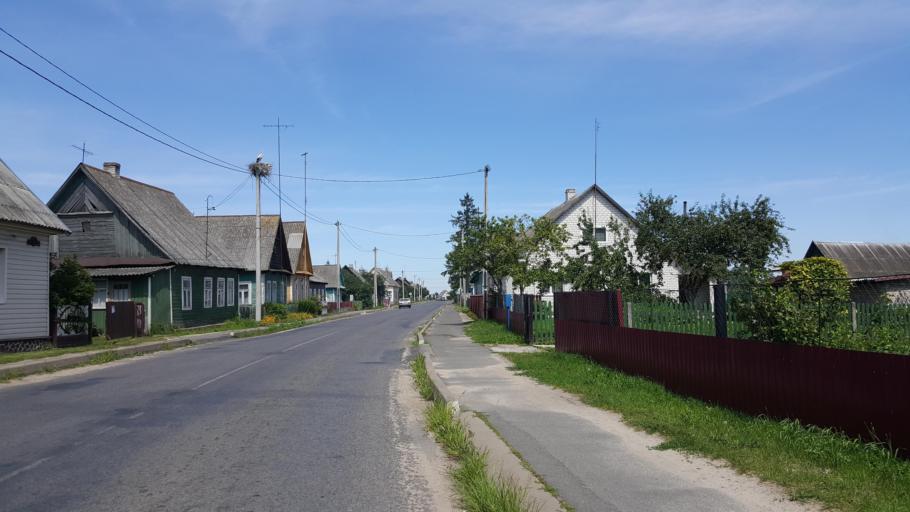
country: BY
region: Brest
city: Pruzhany
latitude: 52.5586
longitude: 24.2157
